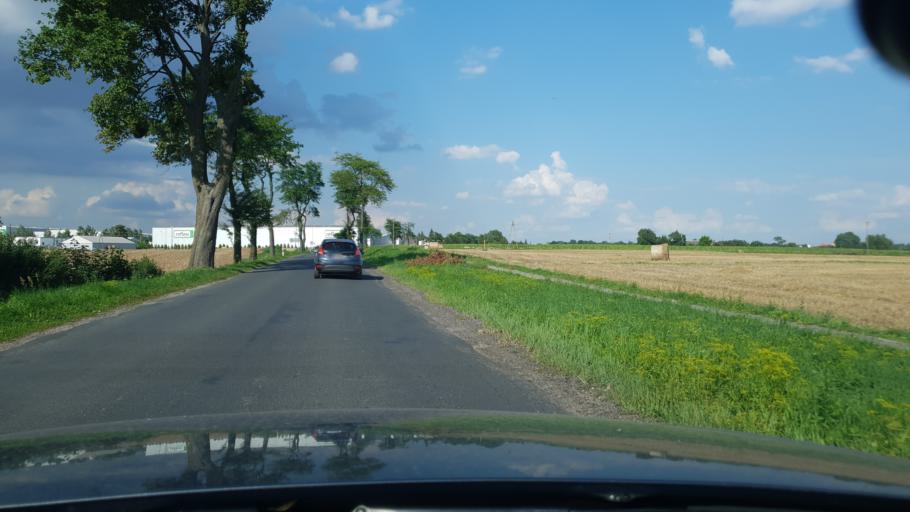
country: PL
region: Kujawsko-Pomorskie
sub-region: Powiat wabrzeski
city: Wabrzezno
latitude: 53.2720
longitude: 18.9168
